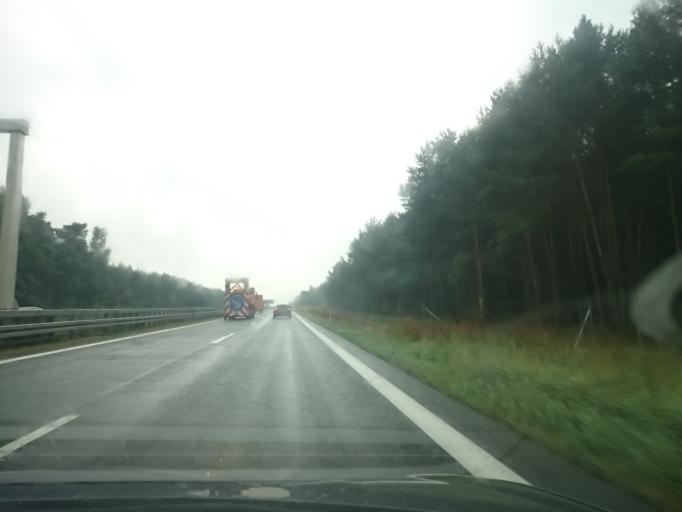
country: DE
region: Brandenburg
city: Kremmen
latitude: 52.6990
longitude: 13.0104
